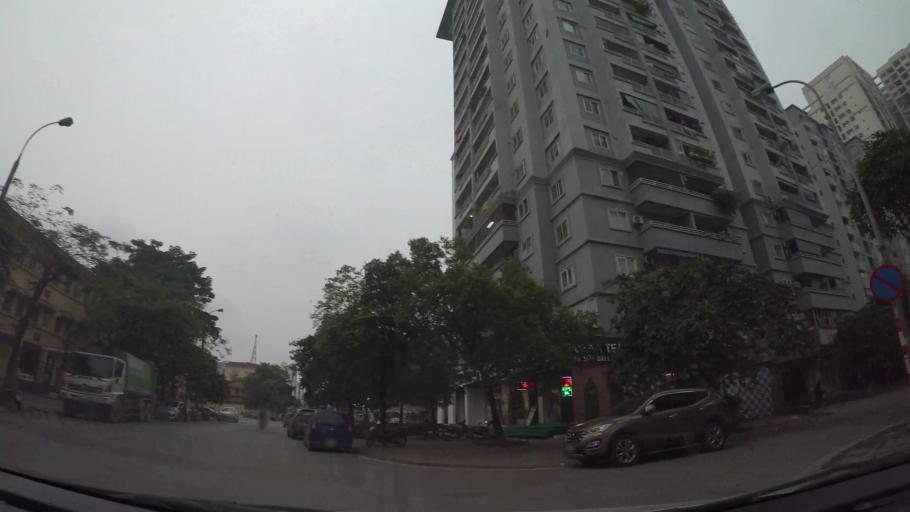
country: VN
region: Ha Noi
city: Cau Dien
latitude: 21.0367
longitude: 105.7660
